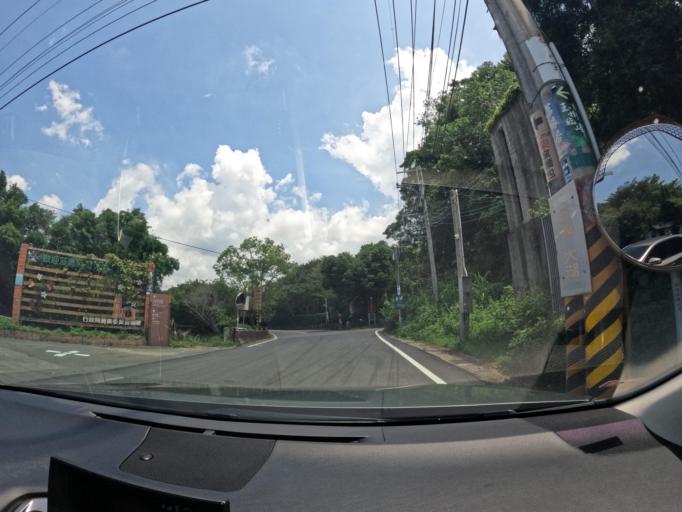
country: TW
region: Taiwan
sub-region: Miaoli
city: Miaoli
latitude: 24.4085
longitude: 120.7873
